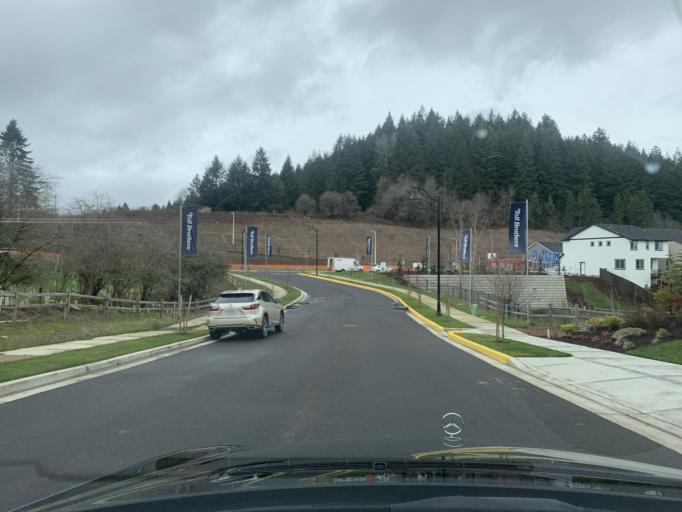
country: US
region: Oregon
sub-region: Clackamas County
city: Happy Valley
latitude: 45.4407
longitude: -122.5097
